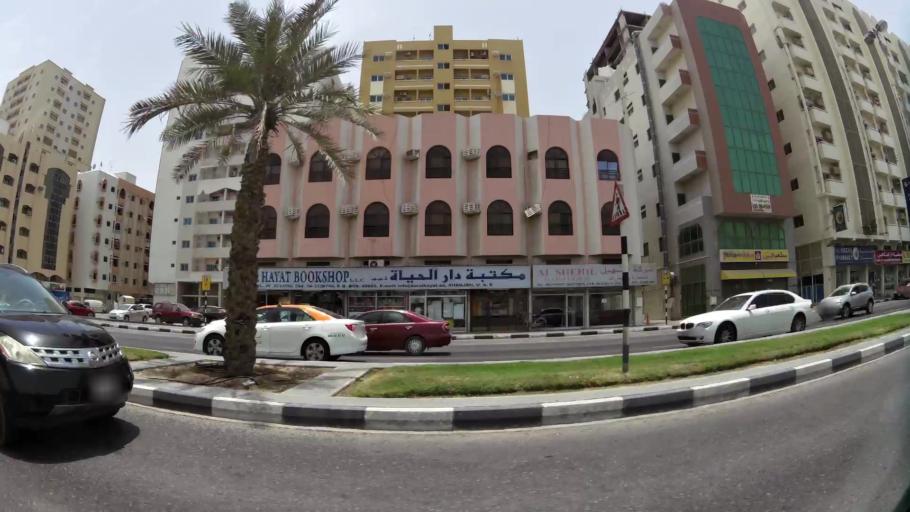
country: AE
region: Ash Shariqah
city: Sharjah
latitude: 25.3503
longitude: 55.3944
